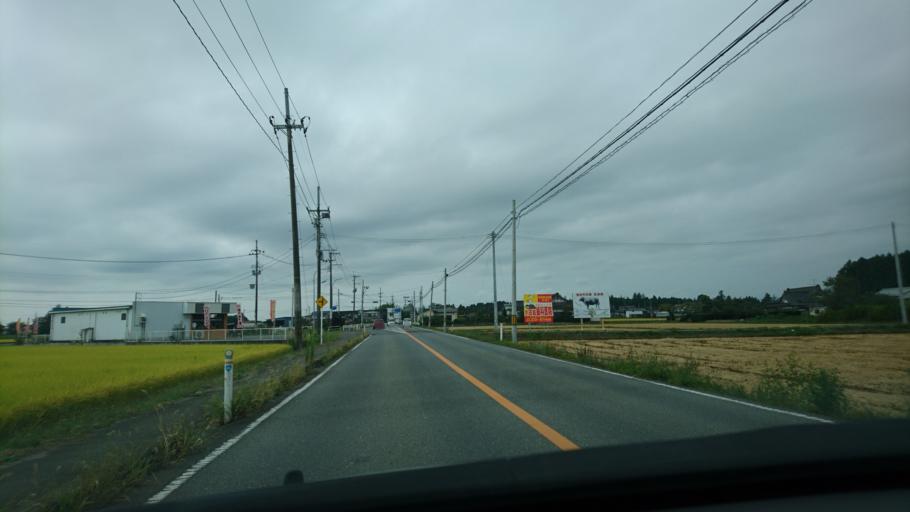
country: JP
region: Iwate
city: Ichinoseki
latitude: 38.7486
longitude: 141.0531
